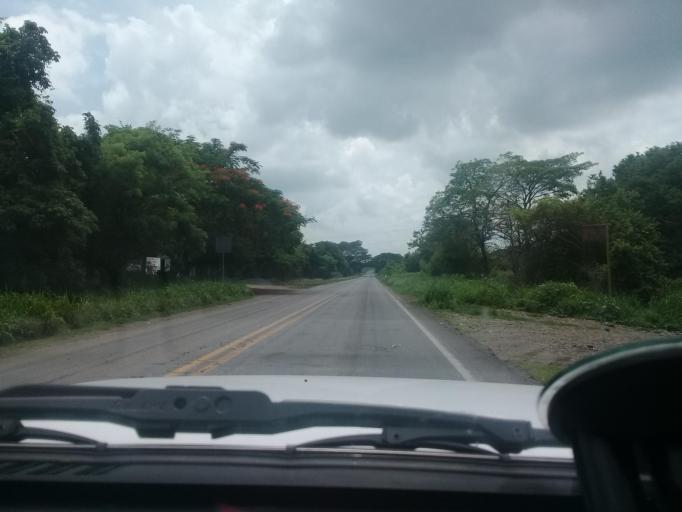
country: MX
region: Veracruz
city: Paso de Ovejas
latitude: 19.2913
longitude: -96.4519
